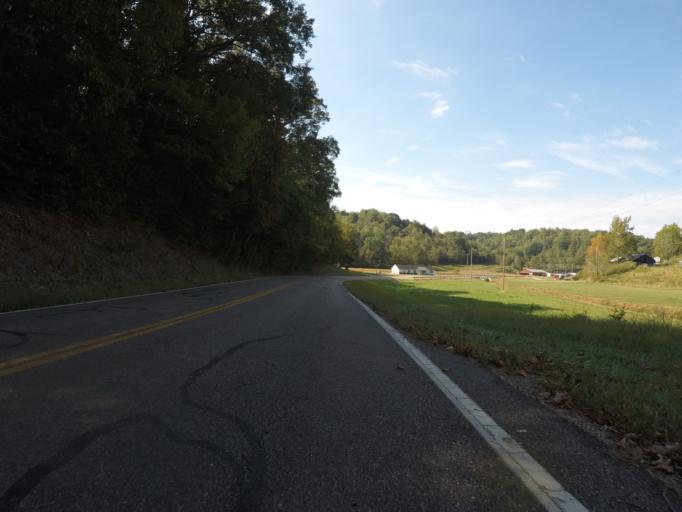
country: US
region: West Virginia
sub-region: Cabell County
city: Lesage
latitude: 38.6323
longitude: -82.4329
